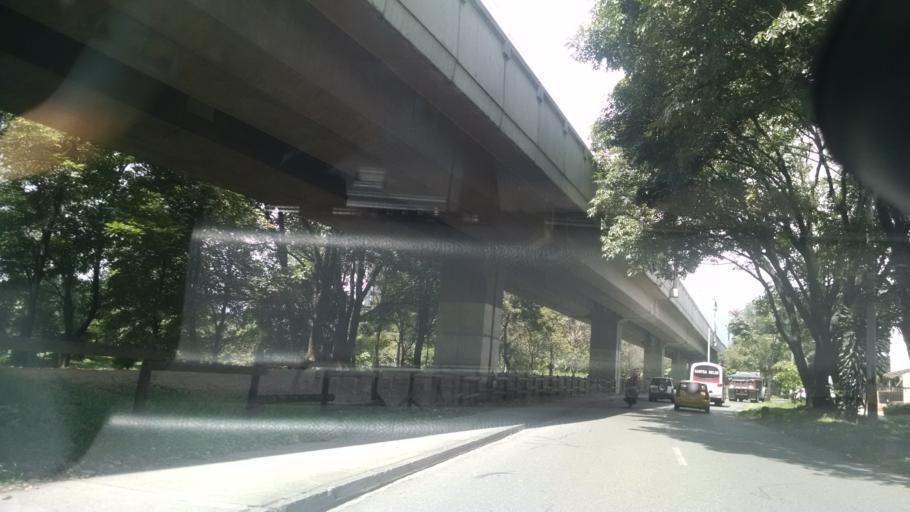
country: CO
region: Antioquia
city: Medellin
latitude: 6.2534
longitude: -75.5846
